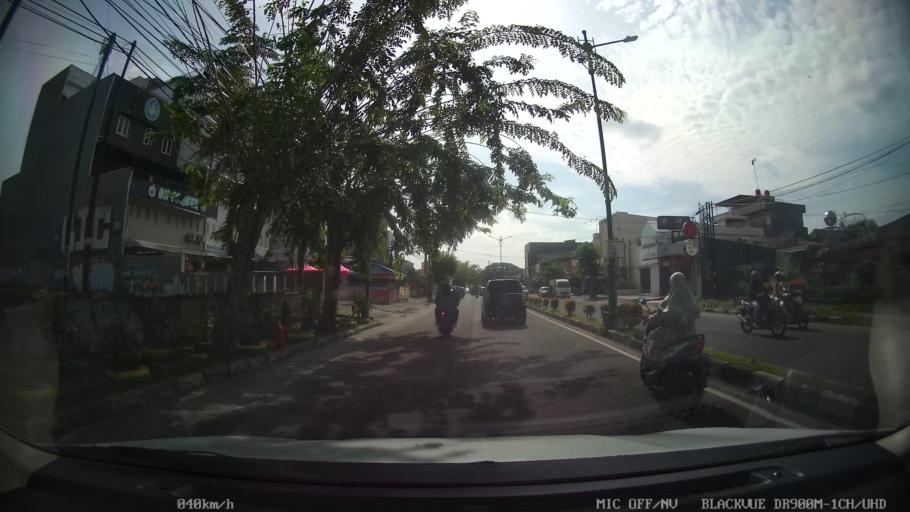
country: ID
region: North Sumatra
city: Medan
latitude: 3.5675
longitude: 98.6503
